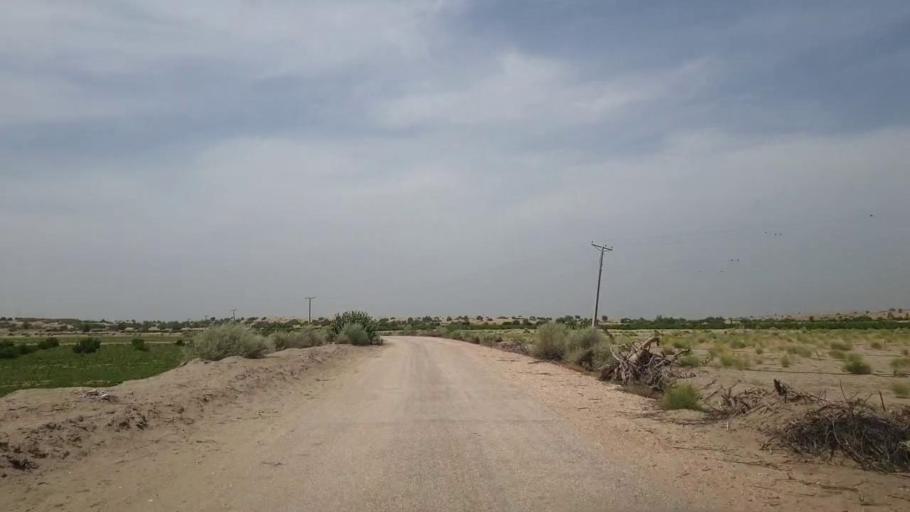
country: PK
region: Sindh
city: Kot Diji
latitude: 27.0847
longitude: 69.0731
